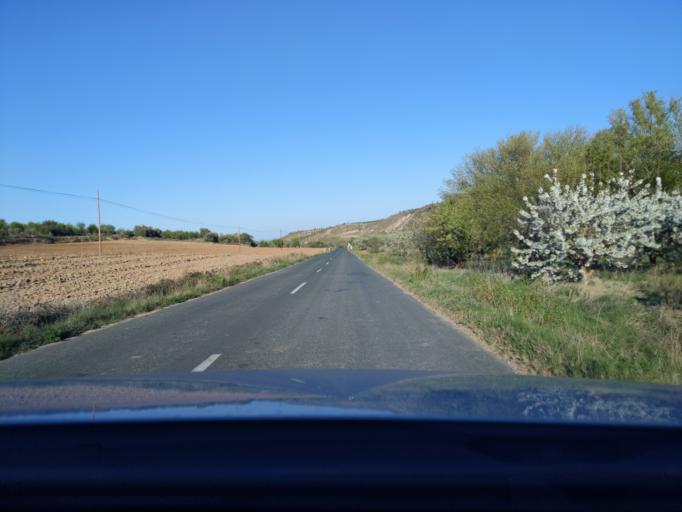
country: ES
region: La Rioja
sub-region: Provincia de La Rioja
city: Bergasa
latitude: 42.2553
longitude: -2.1213
